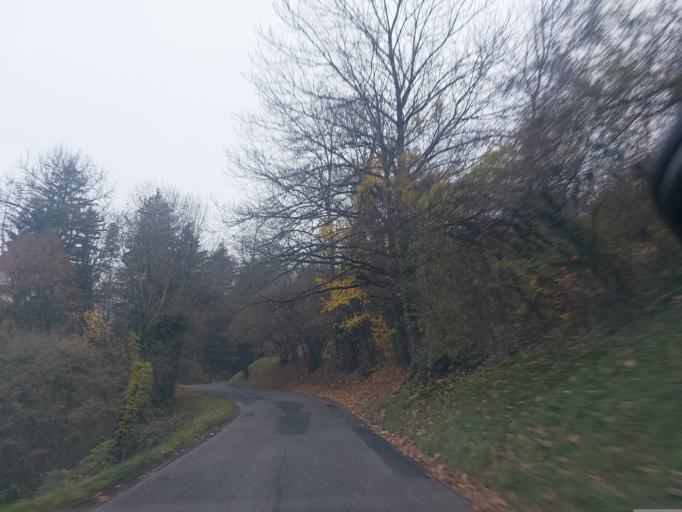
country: CH
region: Vaud
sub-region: Riviera-Pays-d'Enhaut District
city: Blonay
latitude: 46.4925
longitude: 6.8763
